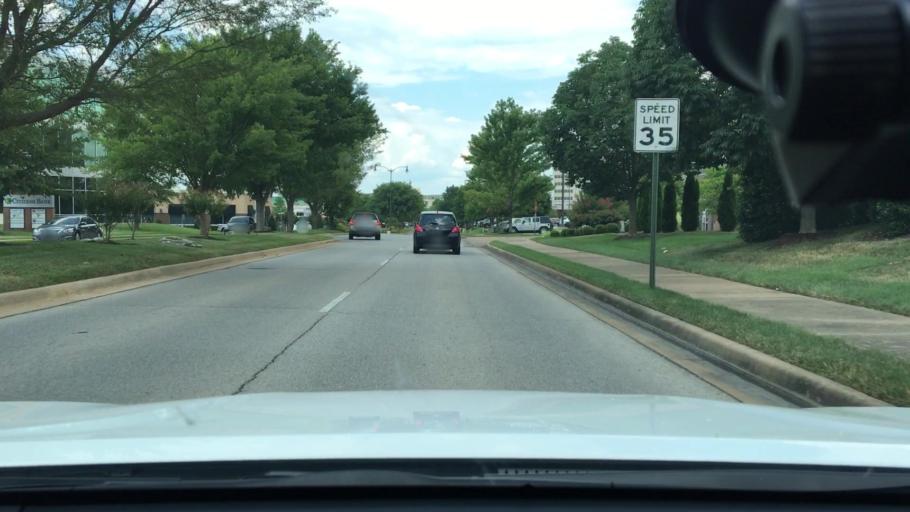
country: US
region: Arkansas
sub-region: Benton County
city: Cave Springs
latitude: 36.3039
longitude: -94.1888
